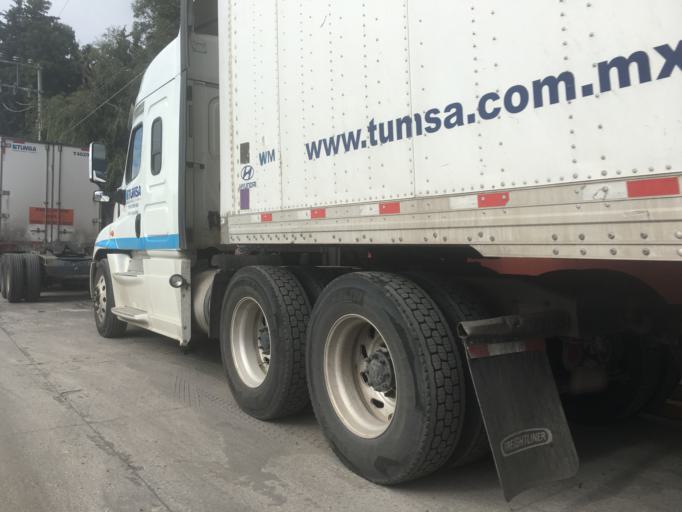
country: MX
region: Mexico
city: Santa Maria Totoltepec
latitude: 19.2912
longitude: -99.5938
